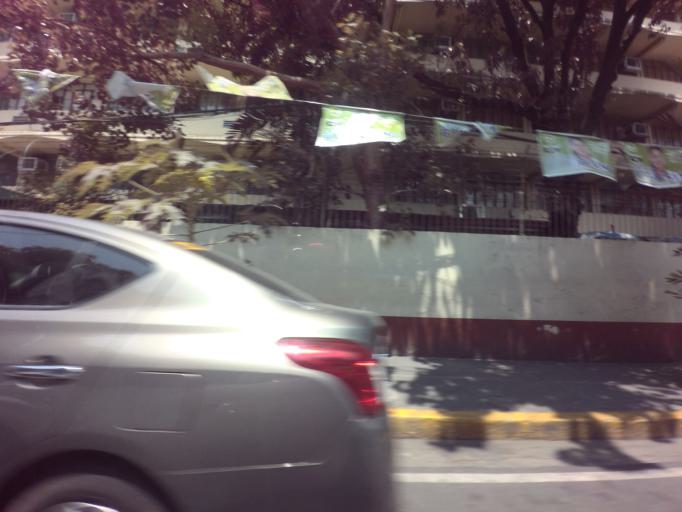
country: PH
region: Metro Manila
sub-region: City of Manila
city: Port Area
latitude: 14.5649
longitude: 120.9971
